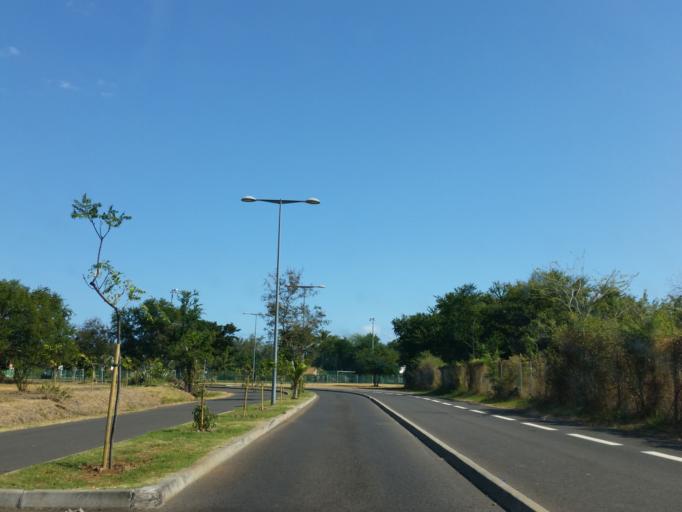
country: RE
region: Reunion
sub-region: Reunion
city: Saint-Paul
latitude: -20.9806
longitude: 55.2897
